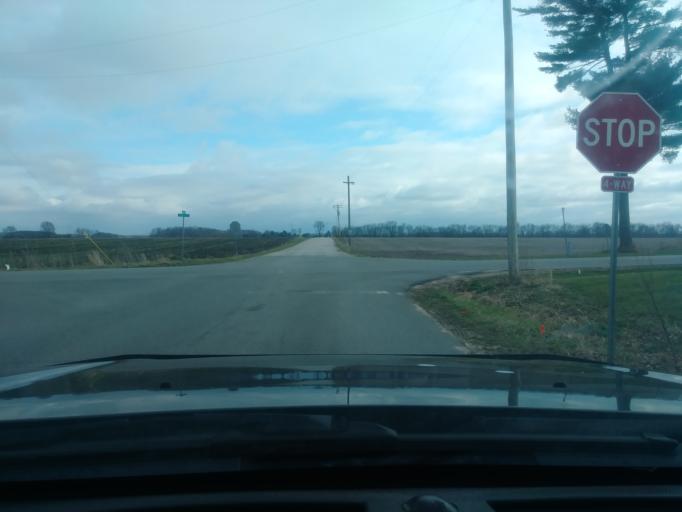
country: US
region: Indiana
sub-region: LaPorte County
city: LaPorte
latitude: 41.5671
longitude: -86.7984
